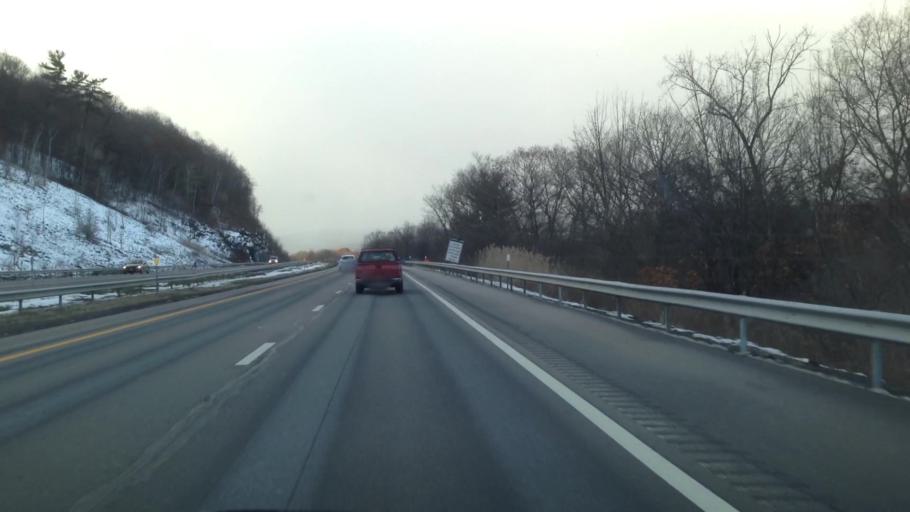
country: US
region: New York
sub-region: Schenectady County
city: Scotia
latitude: 42.8606
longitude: -74.0368
